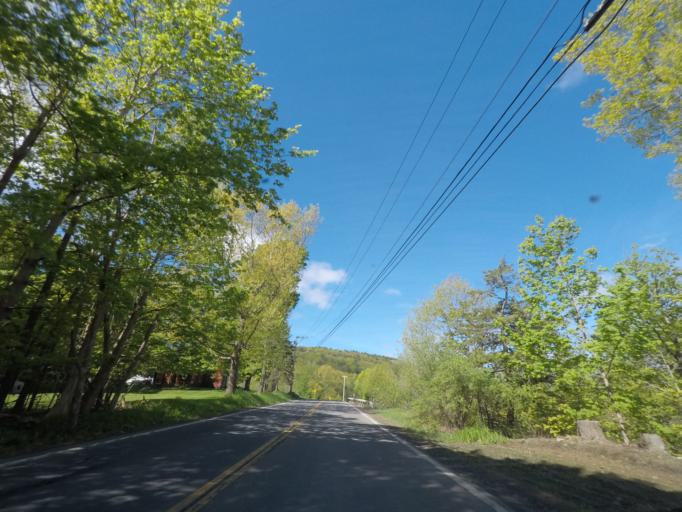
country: US
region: New York
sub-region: Albany County
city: Ravena
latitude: 42.4678
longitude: -73.8805
